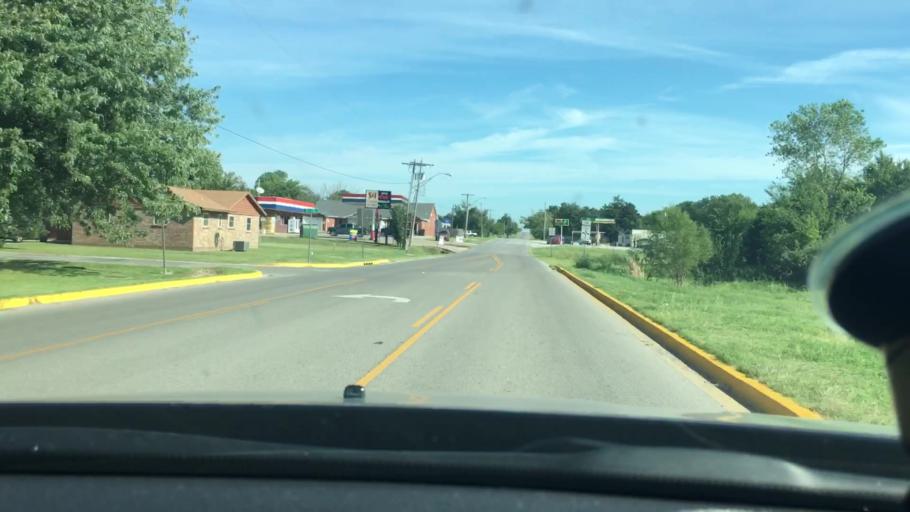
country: US
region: Oklahoma
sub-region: Carter County
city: Lone Grove
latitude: 34.1794
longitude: -97.2474
